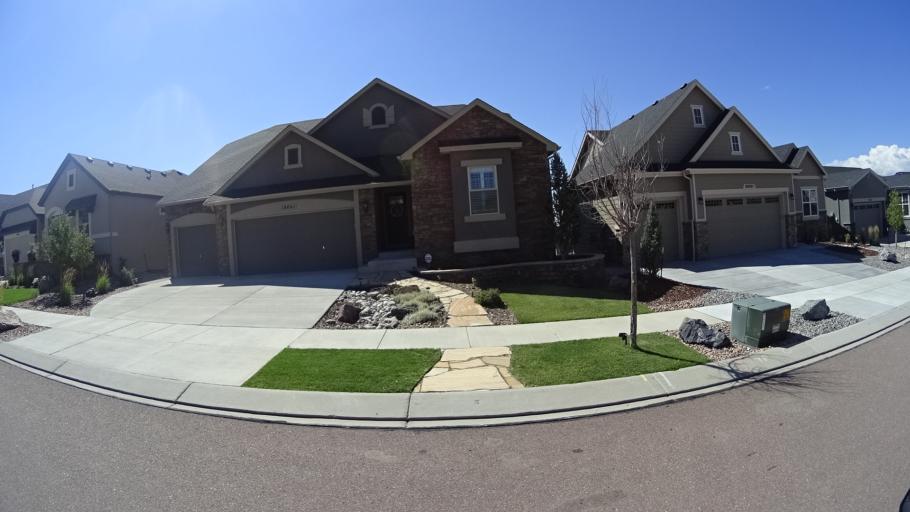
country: US
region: Colorado
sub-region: El Paso County
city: Black Forest
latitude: 38.9770
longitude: -104.7397
